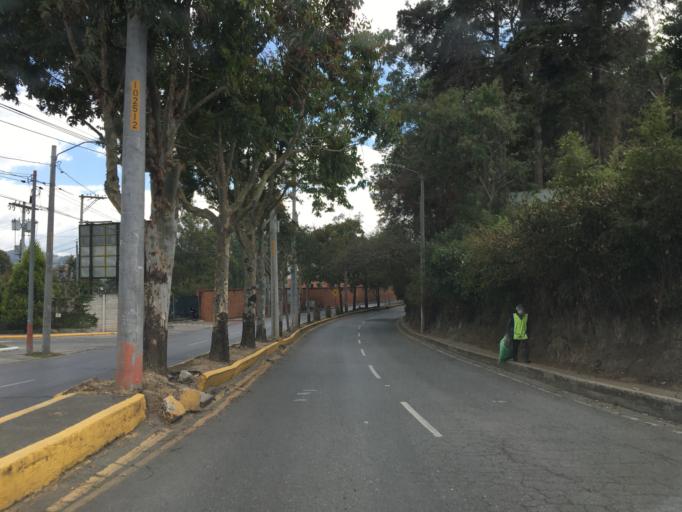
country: GT
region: Guatemala
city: Guatemala City
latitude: 14.6173
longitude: -90.4729
